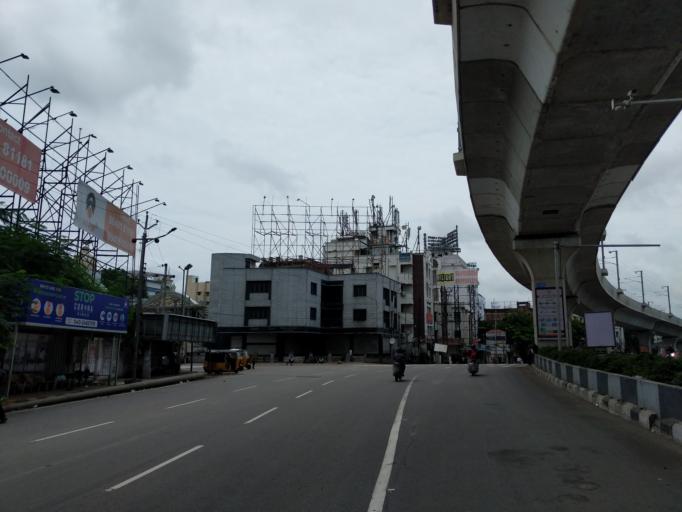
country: IN
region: Telangana
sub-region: Hyderabad
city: Hyderabad
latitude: 17.3965
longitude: 78.4711
